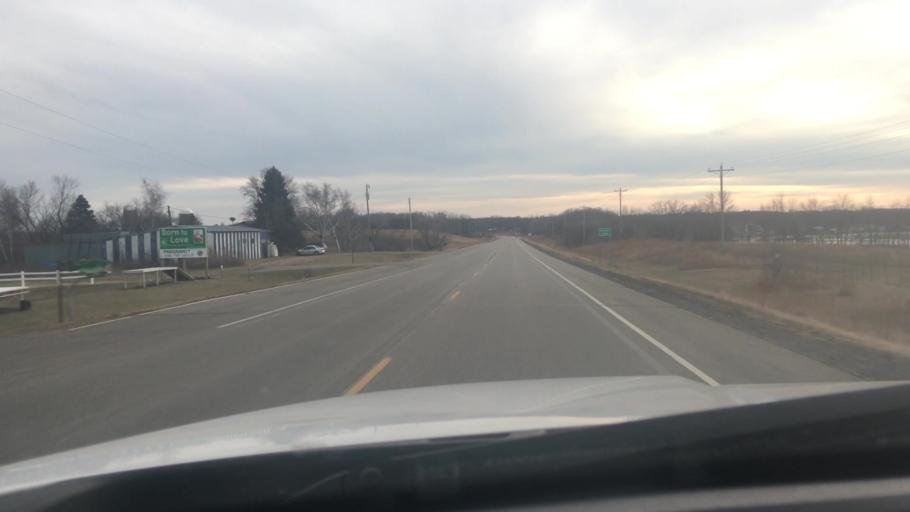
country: US
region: Minnesota
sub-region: Otter Tail County
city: Perham
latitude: 46.3027
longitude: -95.7182
